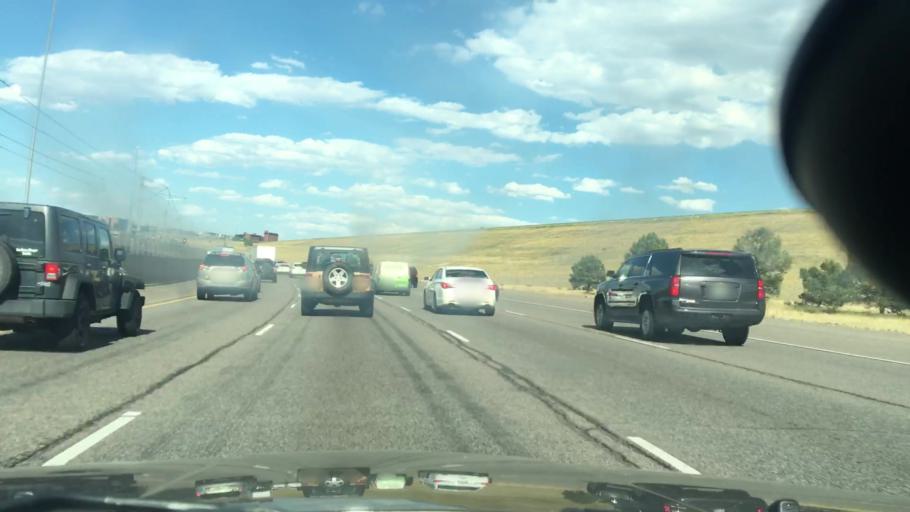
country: US
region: Colorado
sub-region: Arapahoe County
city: Centennial
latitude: 39.6459
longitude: -104.8686
